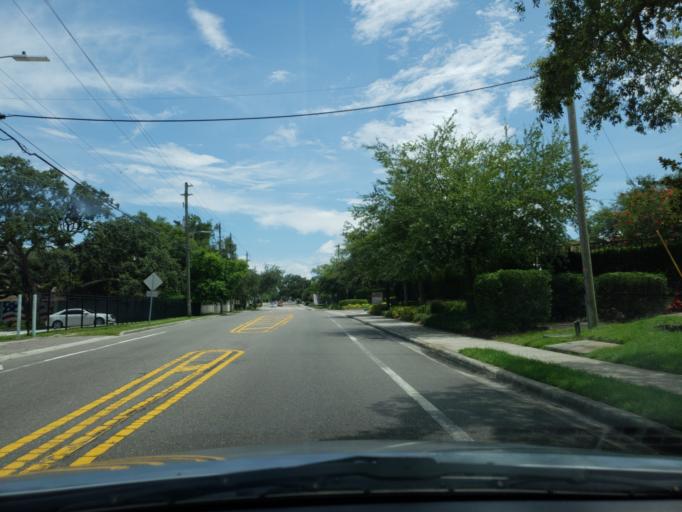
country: US
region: Florida
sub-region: Hillsborough County
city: University
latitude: 28.0730
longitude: -82.4140
